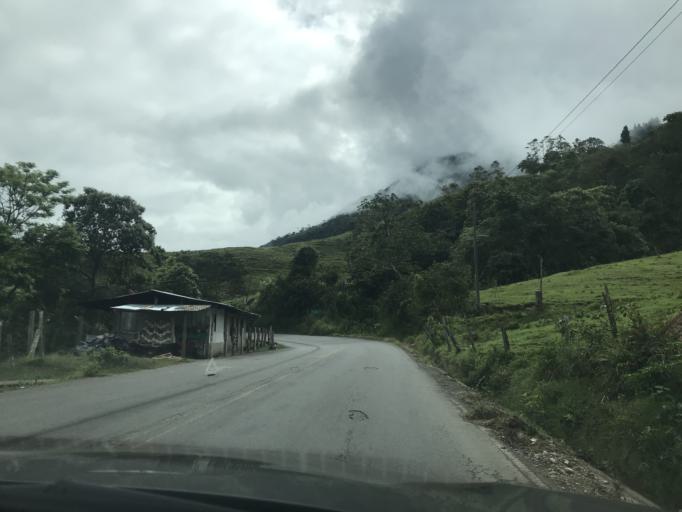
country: PE
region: Pasco
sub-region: Provincia de Oxapampa
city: Villa Rica
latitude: -10.7106
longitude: -75.3666
